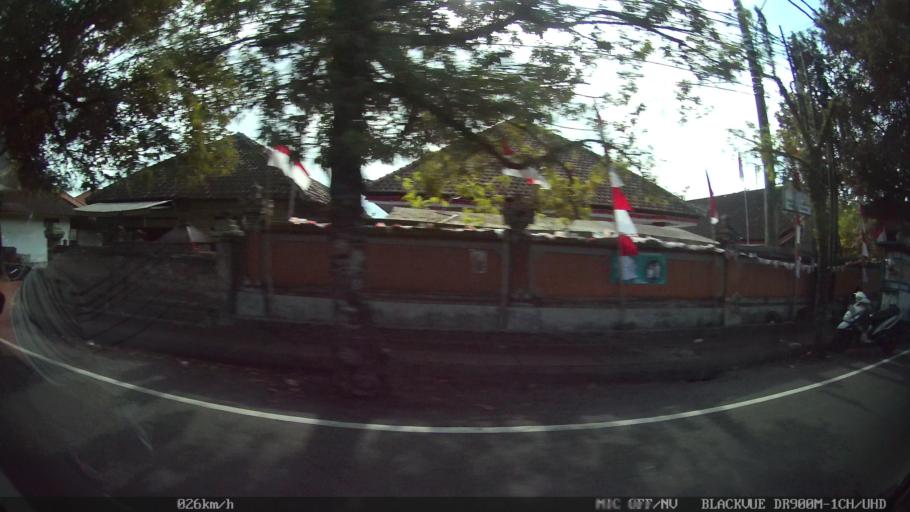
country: ID
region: Bali
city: Tabanan
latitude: -8.5472
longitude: 115.1241
